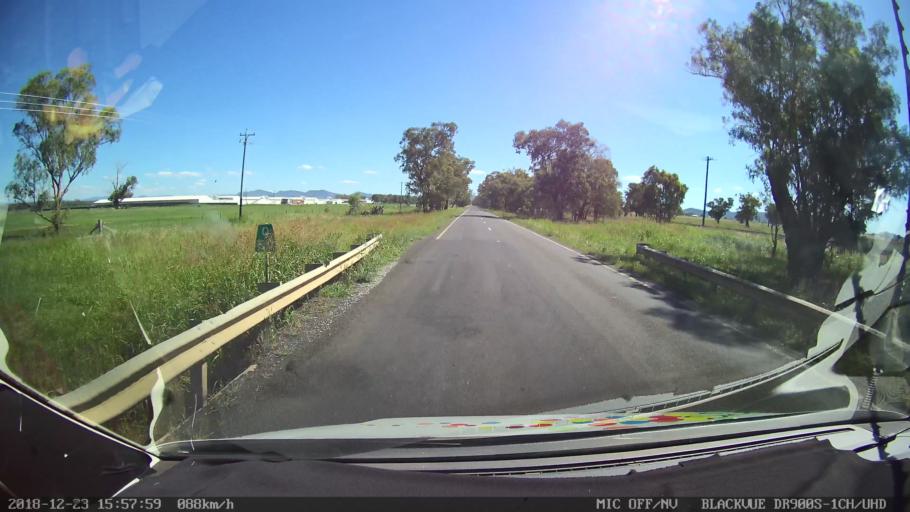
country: AU
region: New South Wales
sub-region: Tamworth Municipality
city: Phillip
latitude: -31.1833
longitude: 150.8454
